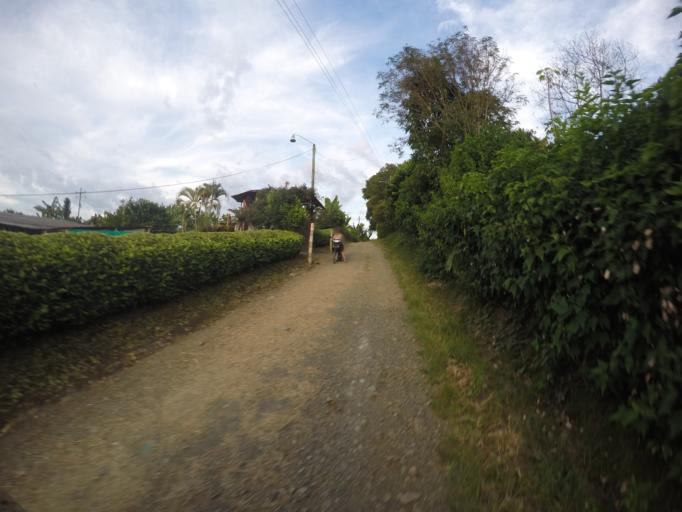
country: CO
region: Valle del Cauca
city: Ulloa
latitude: 4.7129
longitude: -75.7294
